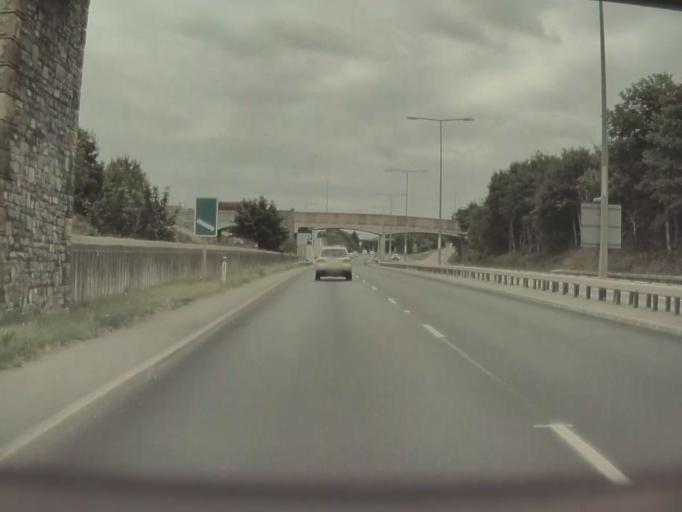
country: GB
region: Wales
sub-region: Anglesey
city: Holyhead
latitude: 53.3026
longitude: -4.6274
